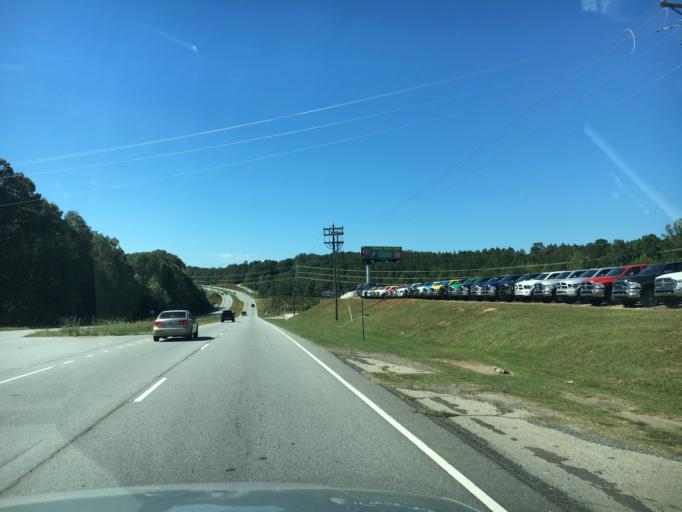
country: US
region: South Carolina
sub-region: Oconee County
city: Utica
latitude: 34.6996
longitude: -82.8889
